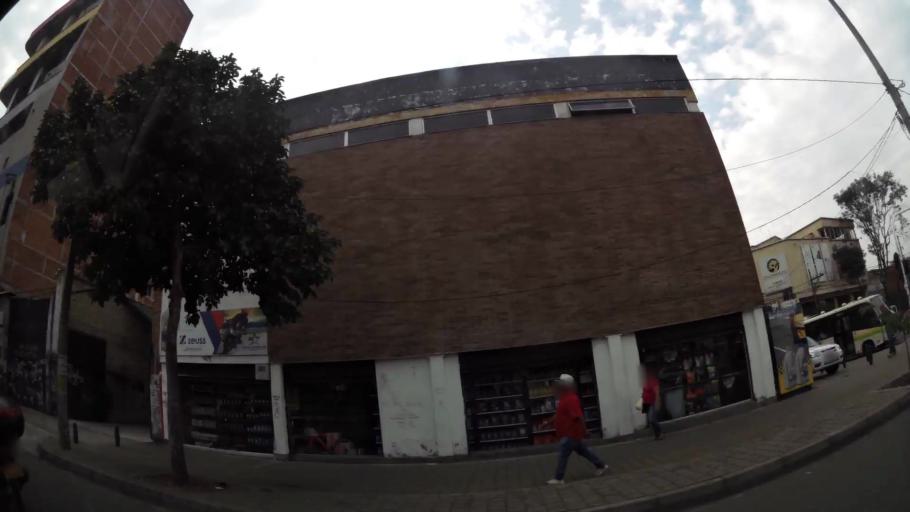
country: CO
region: Antioquia
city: Medellin
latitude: 6.2600
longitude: -75.5696
